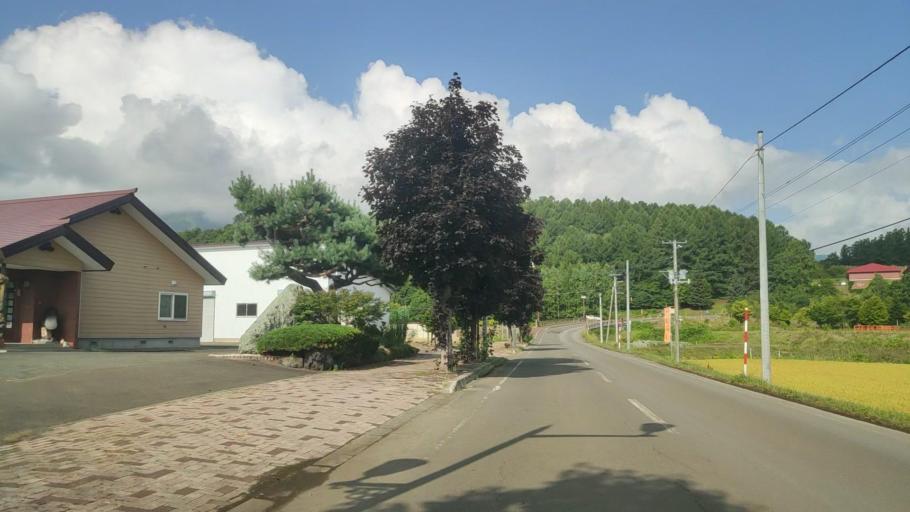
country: JP
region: Hokkaido
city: Shimo-furano
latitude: 43.3572
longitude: 142.3772
